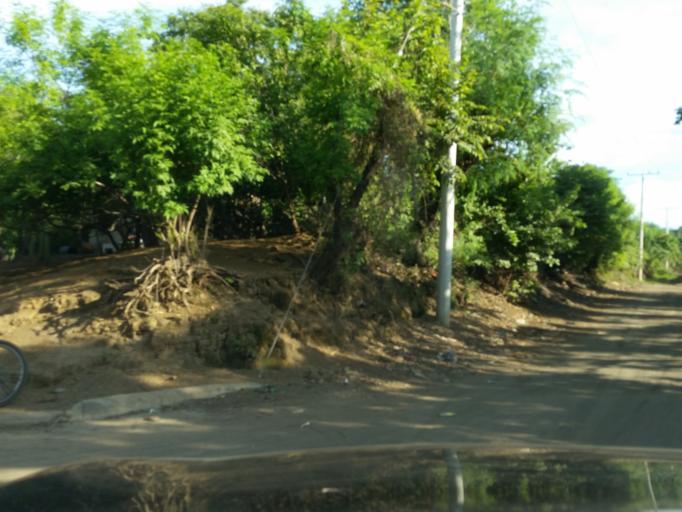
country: NI
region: Managua
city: Managua
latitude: 12.0932
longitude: -86.2024
